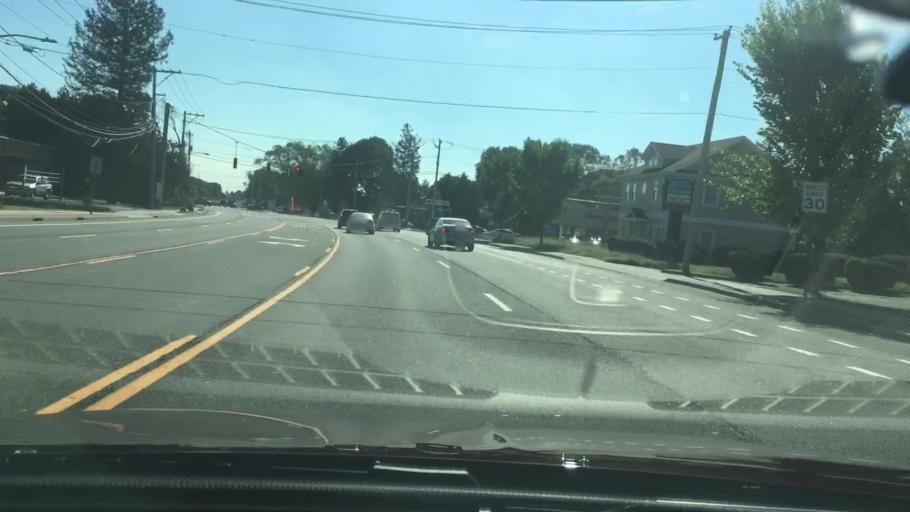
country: US
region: New York
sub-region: Suffolk County
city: Port Jefferson Station
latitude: 40.9295
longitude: -73.0517
